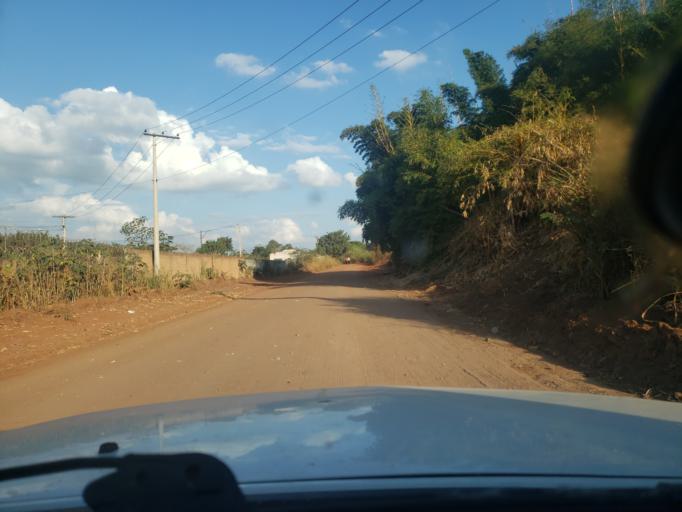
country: BR
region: Sao Paulo
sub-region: Mogi-Mirim
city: Mogi Mirim
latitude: -22.4560
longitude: -46.9421
